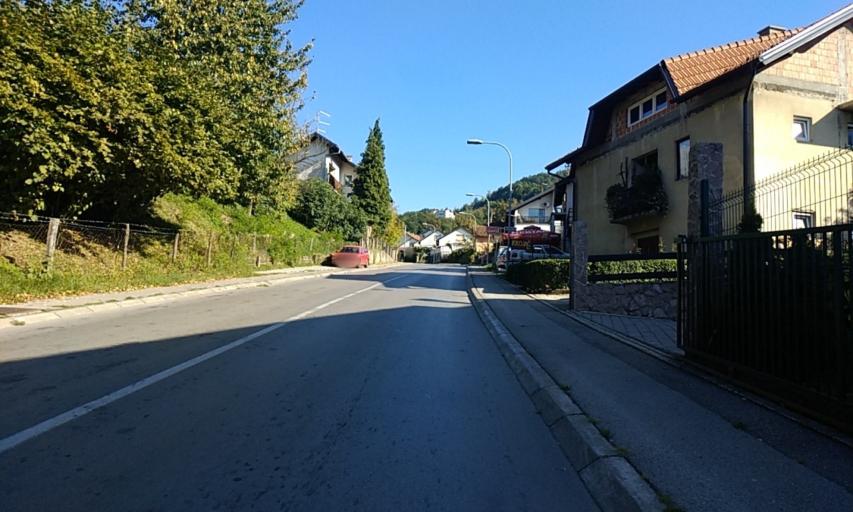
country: BA
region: Republika Srpska
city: Starcevica
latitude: 44.7572
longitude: 17.2076
